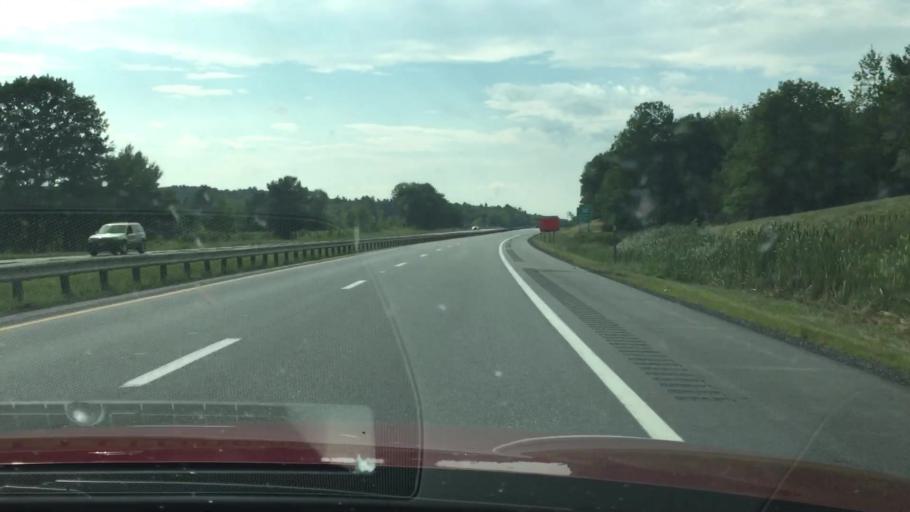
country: US
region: Maine
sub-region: Androscoggin County
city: Lisbon
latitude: 44.0667
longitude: -70.1557
